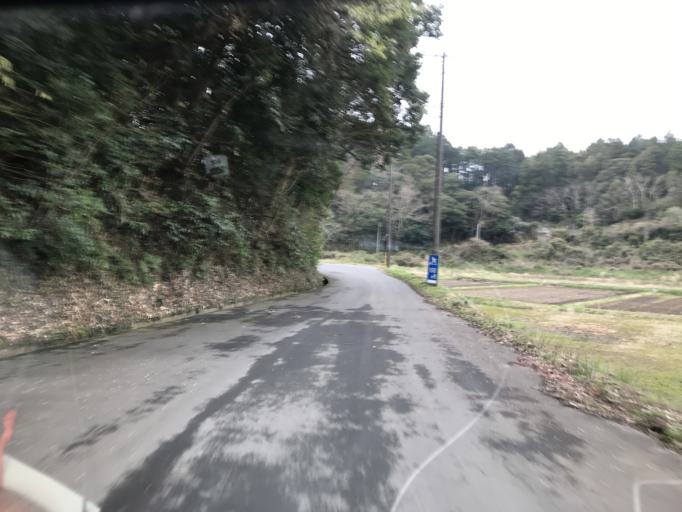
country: JP
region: Chiba
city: Sawara
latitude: 35.8651
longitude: 140.5142
